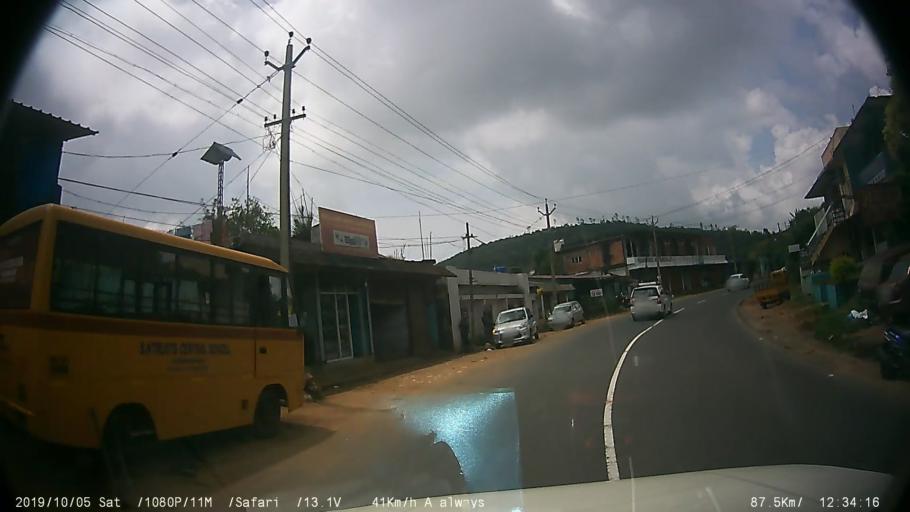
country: IN
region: Tamil Nadu
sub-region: Theni
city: Gudalur
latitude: 9.5777
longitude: 77.0175
